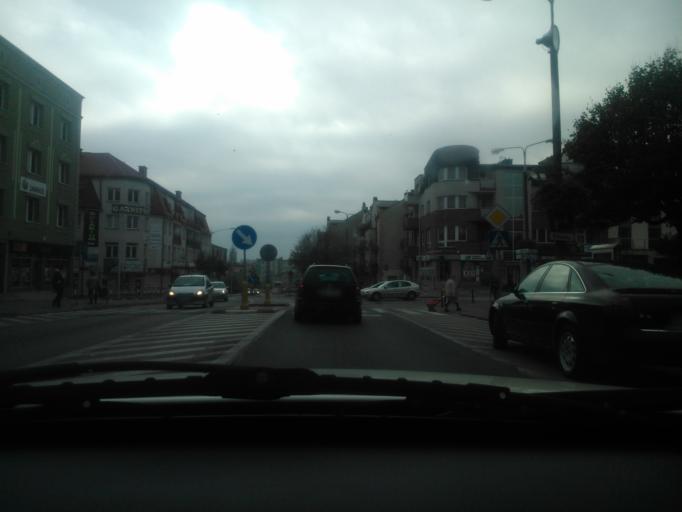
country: PL
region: Masovian Voivodeship
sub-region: Powiat mlawski
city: Mlawa
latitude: 53.1116
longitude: 20.3835
